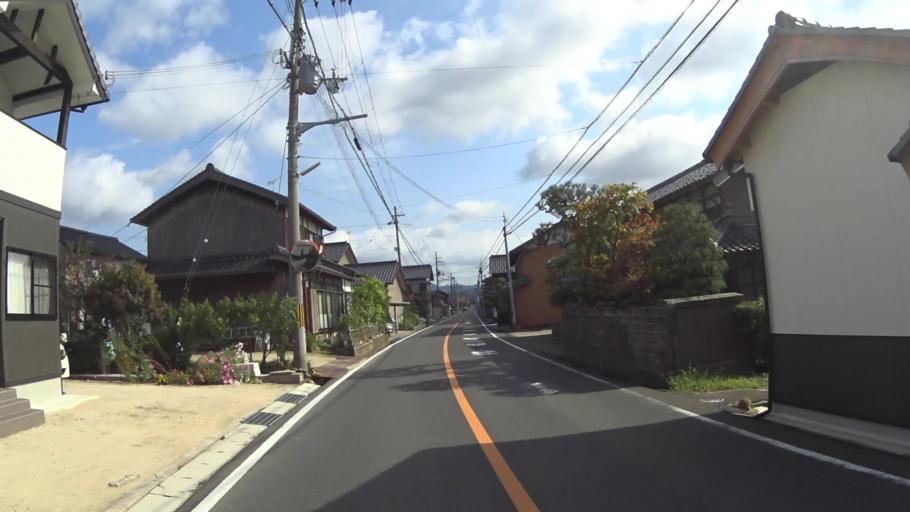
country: JP
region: Kyoto
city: Miyazu
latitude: 35.6088
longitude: 135.0863
